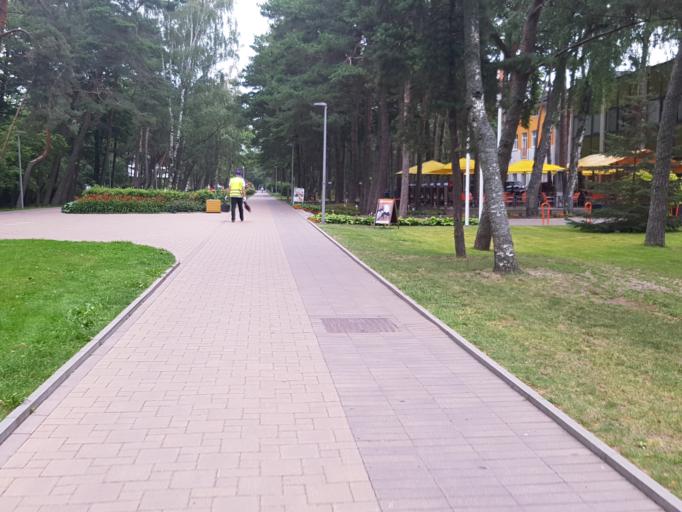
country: LT
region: Klaipedos apskritis
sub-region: Klaipeda
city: Palanga
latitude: 55.9141
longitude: 21.0527
